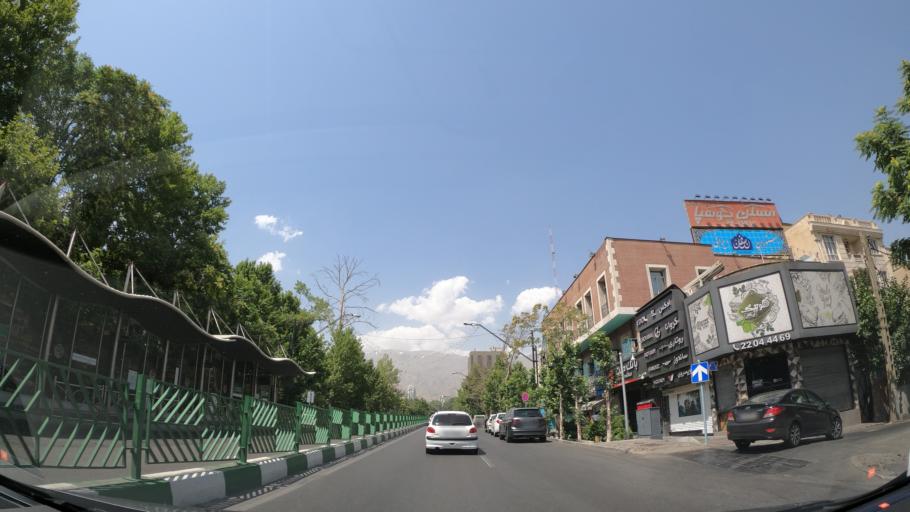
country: IR
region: Tehran
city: Tajrish
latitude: 35.7831
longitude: 51.4146
